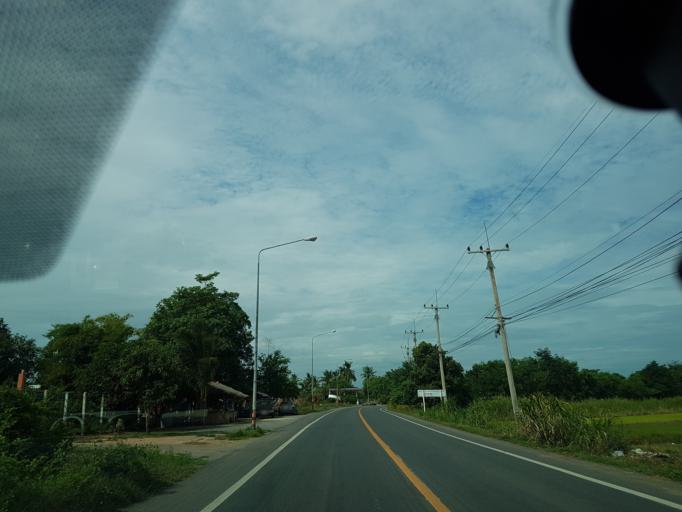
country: TH
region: Lop Buri
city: Tha Wung
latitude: 14.7613
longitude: 100.5631
